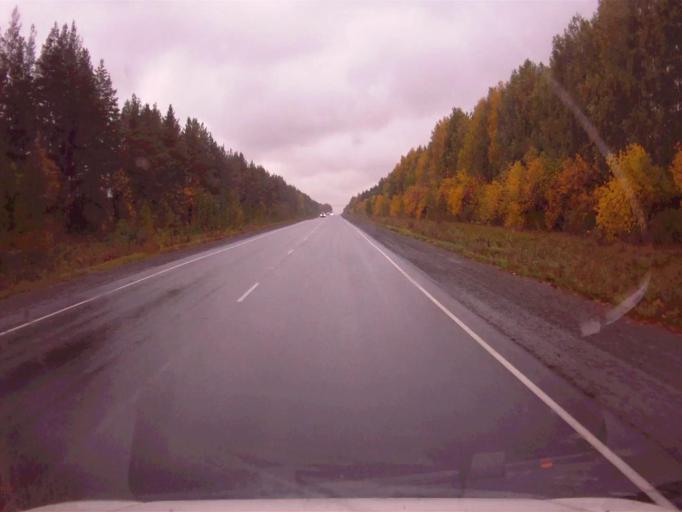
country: RU
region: Chelyabinsk
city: Roshchino
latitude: 55.3766
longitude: 61.1487
